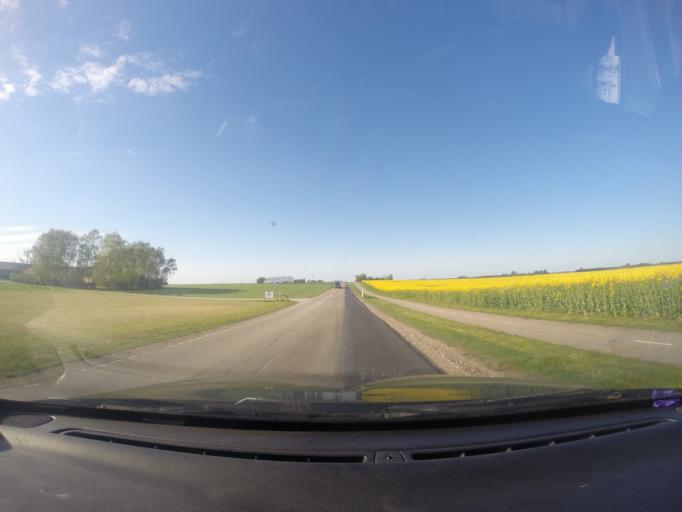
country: DK
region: Capital Region
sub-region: Hoje-Taastrup Kommune
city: Taastrup
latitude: 55.6696
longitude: 12.2537
